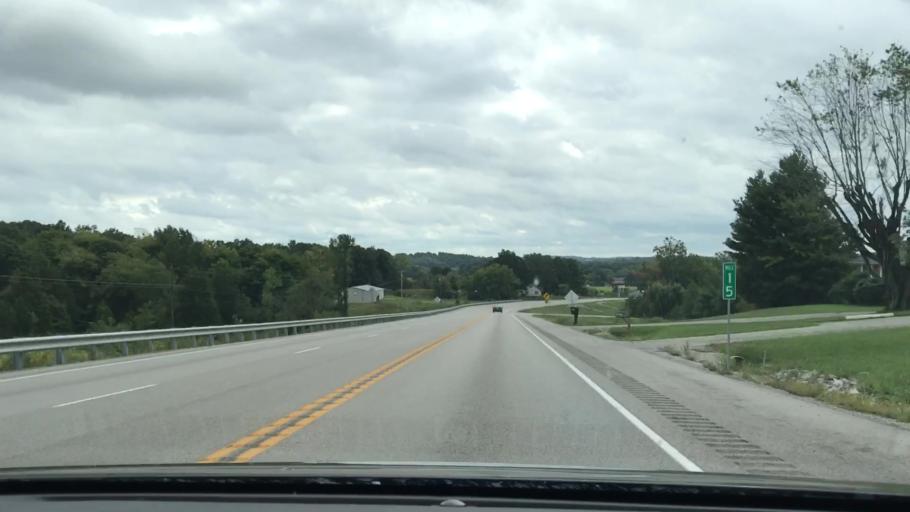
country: US
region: Kentucky
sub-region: Barren County
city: Glasgow
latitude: 36.9490
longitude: -85.8440
